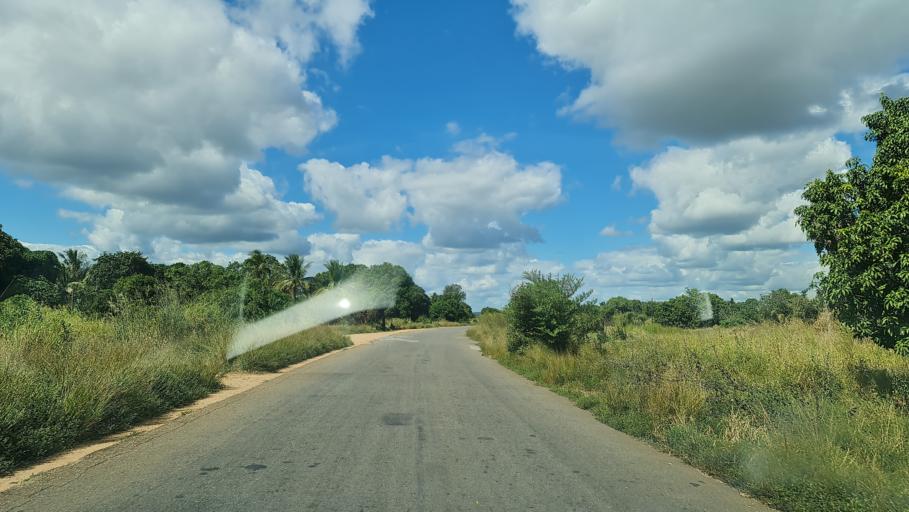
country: MZ
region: Zambezia
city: Quelimane
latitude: -17.5072
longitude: 36.2485
